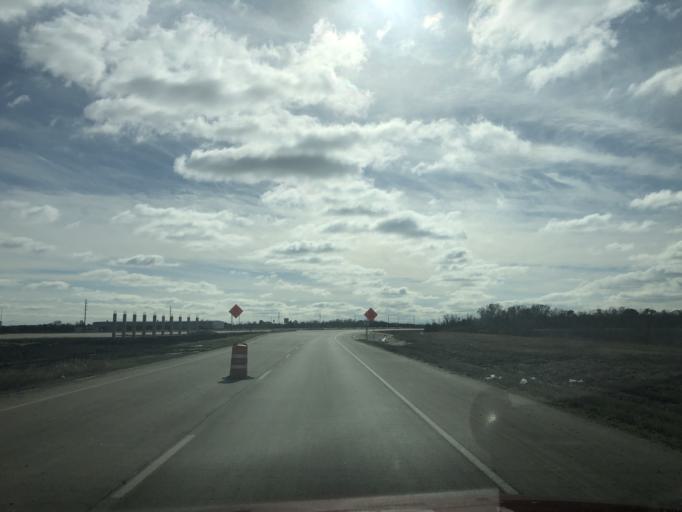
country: US
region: Texas
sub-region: Chambers County
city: Mont Belvieu
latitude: 29.8183
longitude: -94.8632
